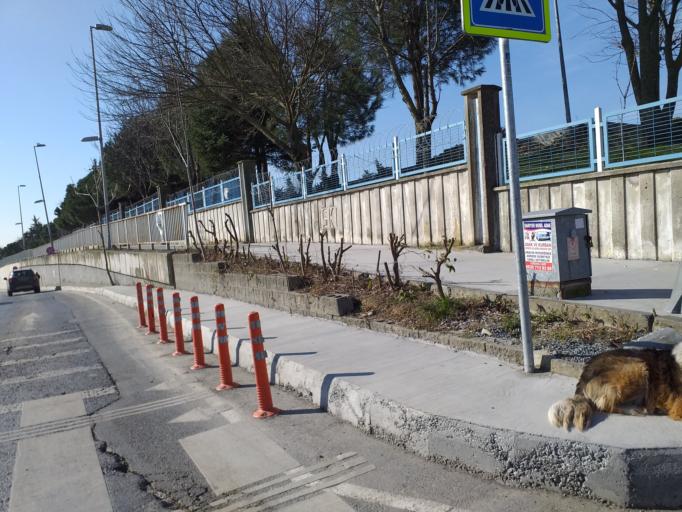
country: TR
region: Istanbul
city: Sisli
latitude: 41.1112
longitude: 29.0294
